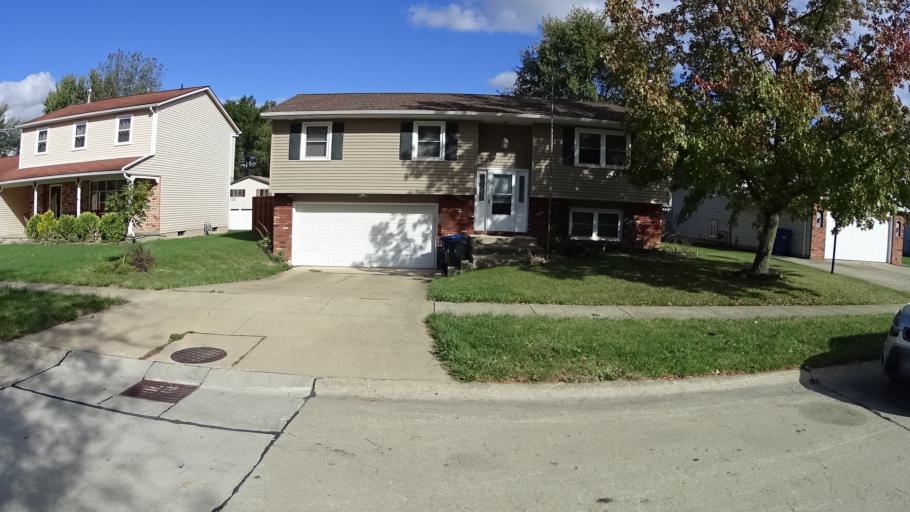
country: US
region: Ohio
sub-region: Lorain County
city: Grafton
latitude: 41.2832
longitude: -82.0577
